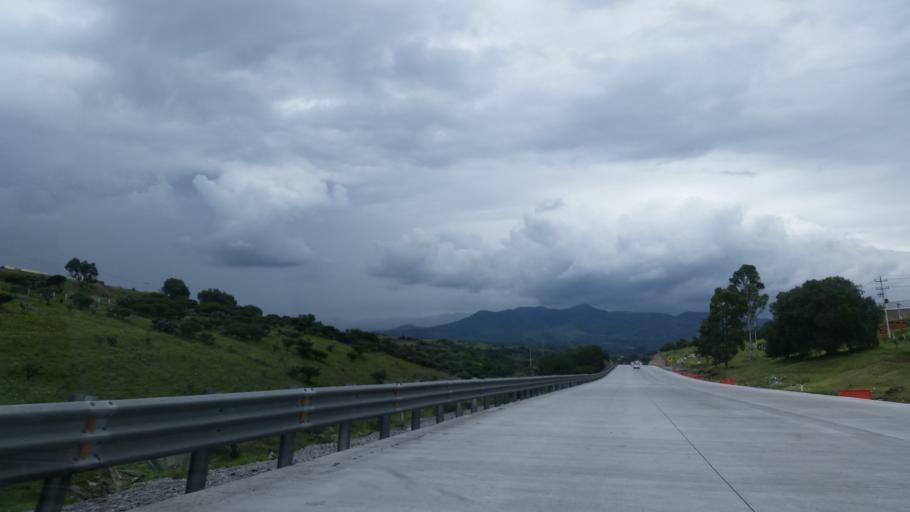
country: MX
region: Hidalgo
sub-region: Tepeji del Rio de Ocampo
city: Cantera de Villagran
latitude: 19.8582
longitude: -99.2983
